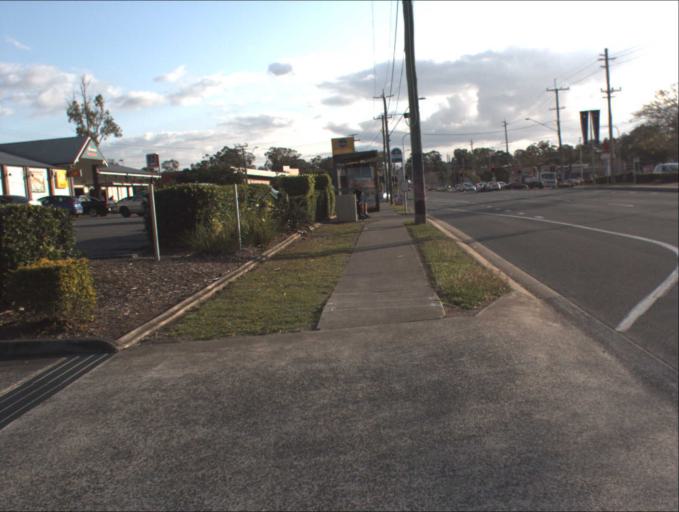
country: AU
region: Queensland
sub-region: Logan
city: Waterford West
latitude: -27.6798
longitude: 153.1170
